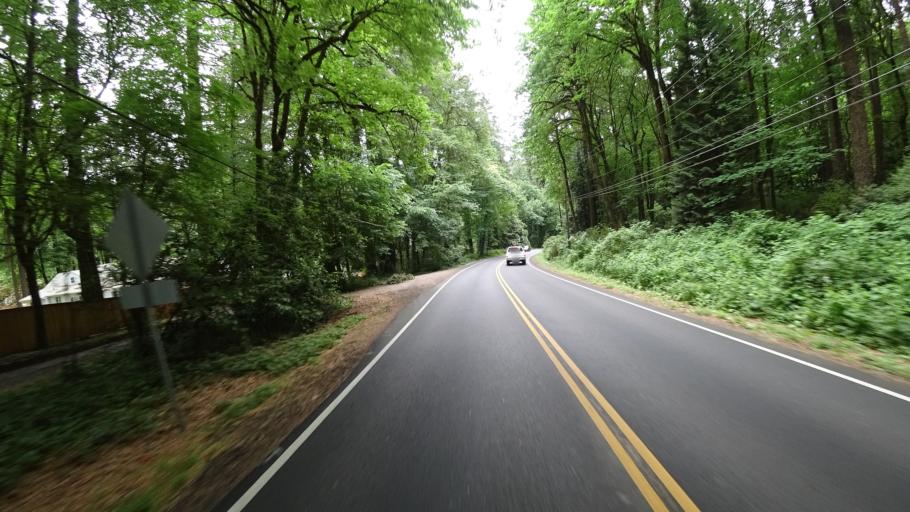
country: US
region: Oregon
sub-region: Clackamas County
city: Lake Oswego
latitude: 45.4289
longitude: -122.6635
